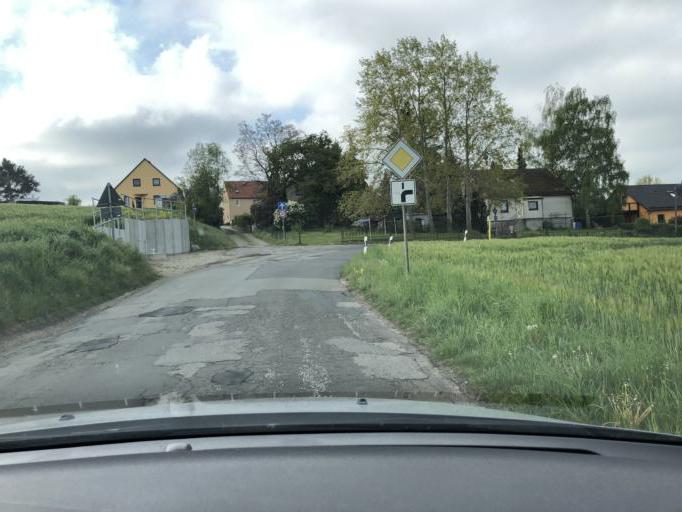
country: DE
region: Thuringia
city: Gerstenberg
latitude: 51.0209
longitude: 12.4399
